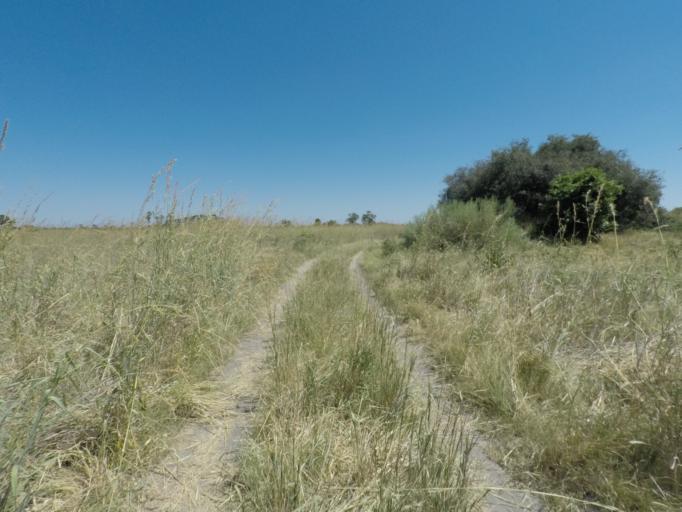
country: BW
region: North West
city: Maun
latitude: -19.4870
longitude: 23.5287
